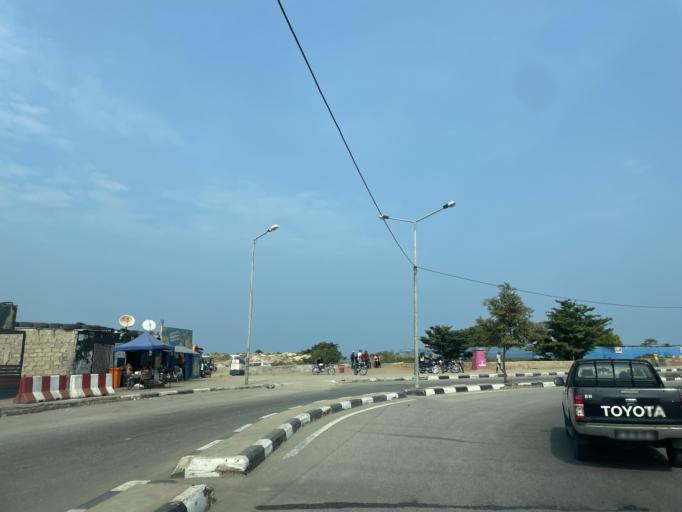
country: AO
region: Luanda
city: Luanda
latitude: -8.8300
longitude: 13.2149
